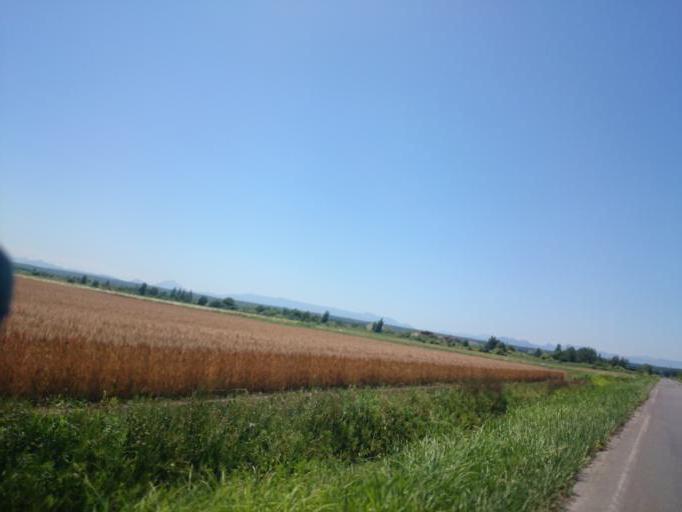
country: JP
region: Hokkaido
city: Ebetsu
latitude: 43.0736
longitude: 141.5681
